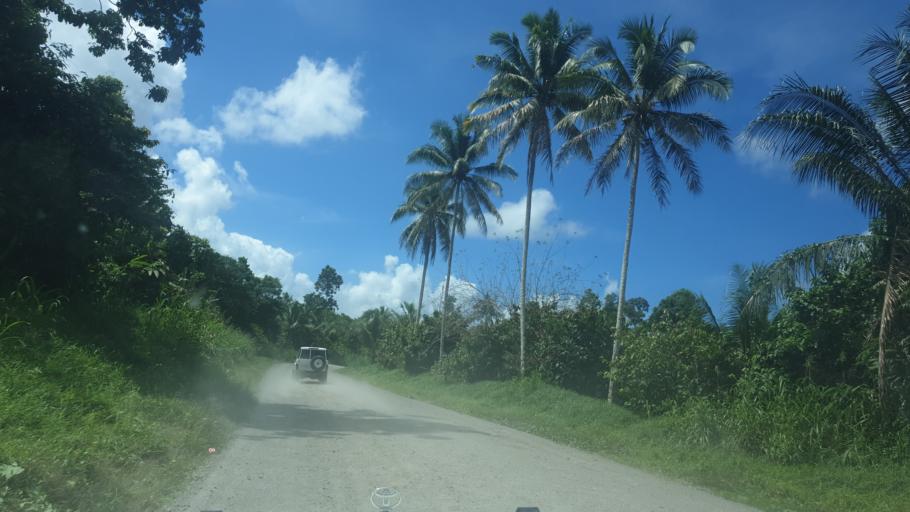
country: PG
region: Bougainville
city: Panguna
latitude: -6.7381
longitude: 155.6668
